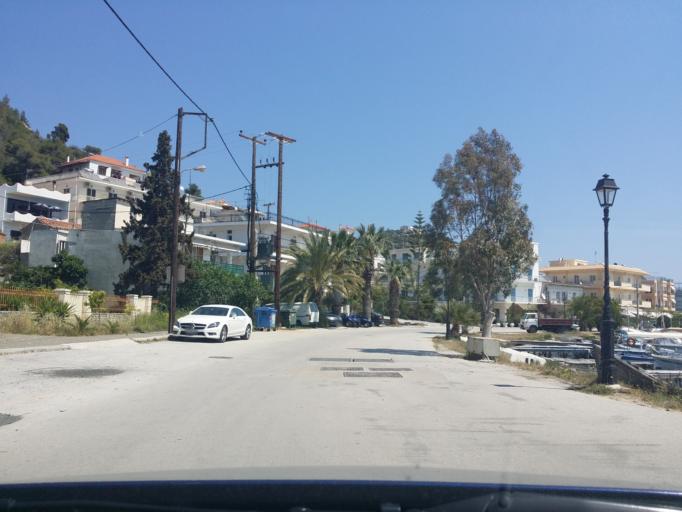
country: GR
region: Attica
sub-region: Nomos Piraios
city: Poros
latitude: 37.5077
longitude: 23.4553
